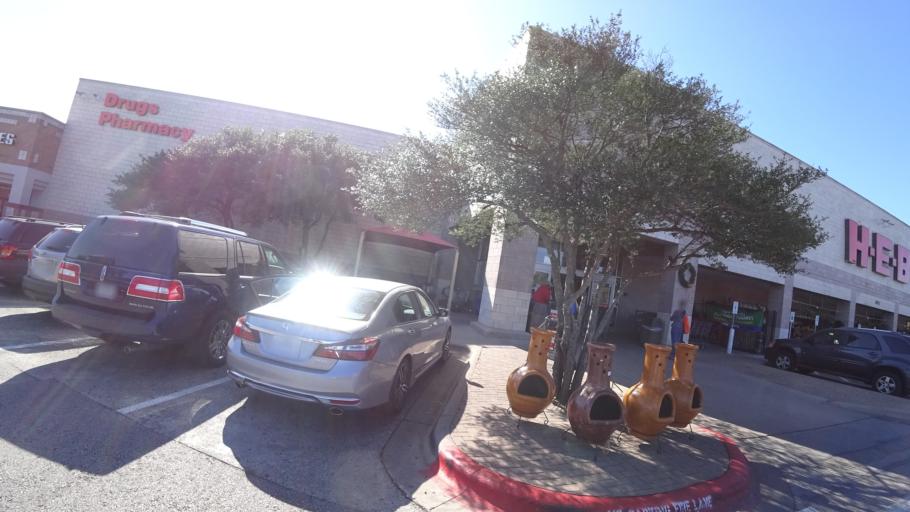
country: US
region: Texas
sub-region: Williamson County
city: Jollyville
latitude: 30.3989
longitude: -97.7480
